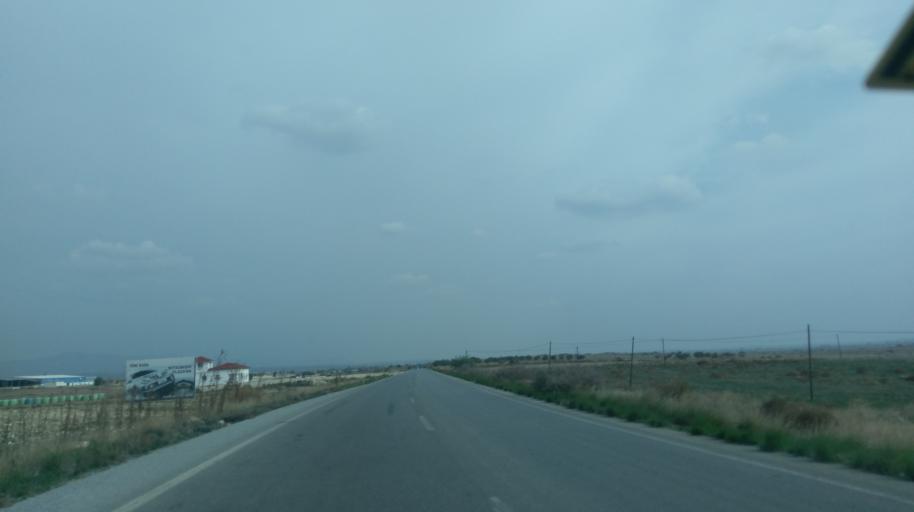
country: CY
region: Ammochostos
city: Lefkonoiko
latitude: 35.2551
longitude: 33.6349
